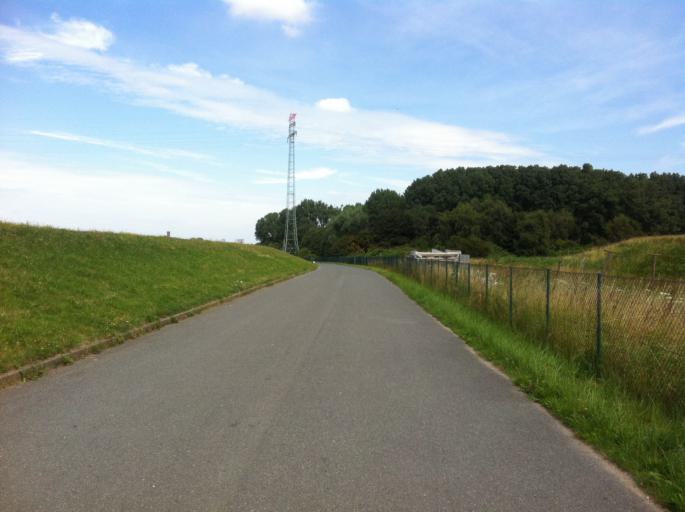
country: DE
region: Hamburg
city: Rothenburgsort
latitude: 53.5171
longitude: 10.0609
